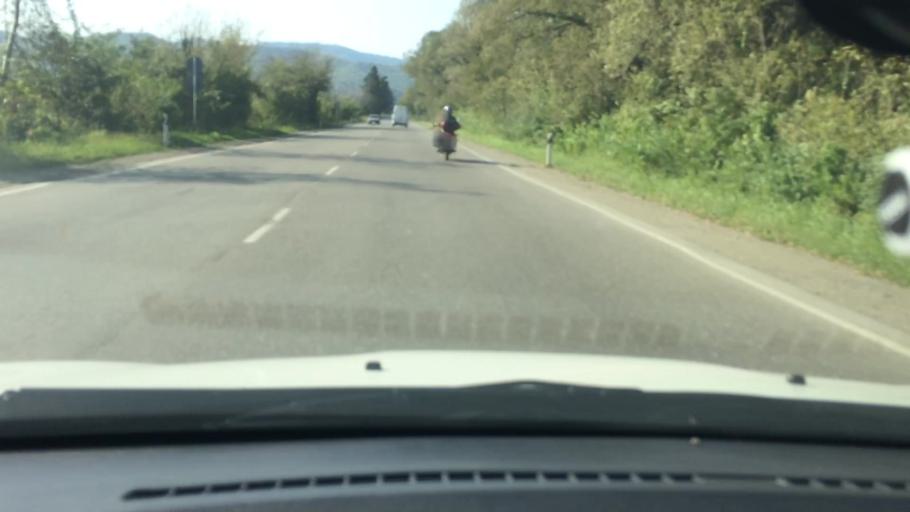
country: GE
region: Imereti
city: Samtredia
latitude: 42.1255
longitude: 42.3348
